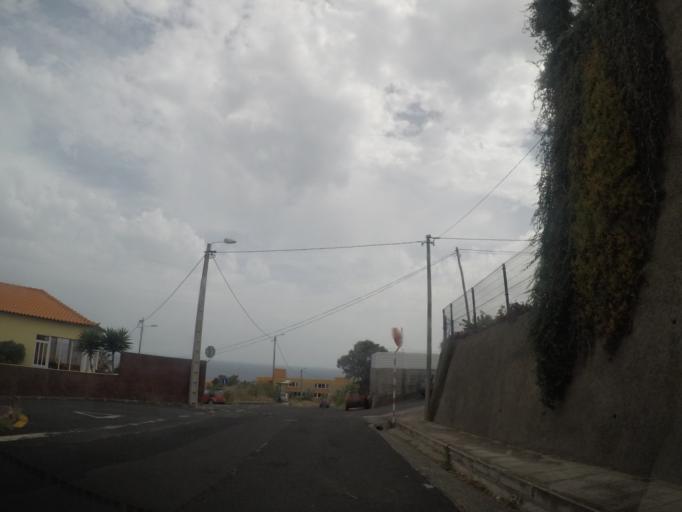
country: PT
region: Madeira
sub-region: Santa Cruz
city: Santa Cruz
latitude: 32.6533
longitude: -16.8187
